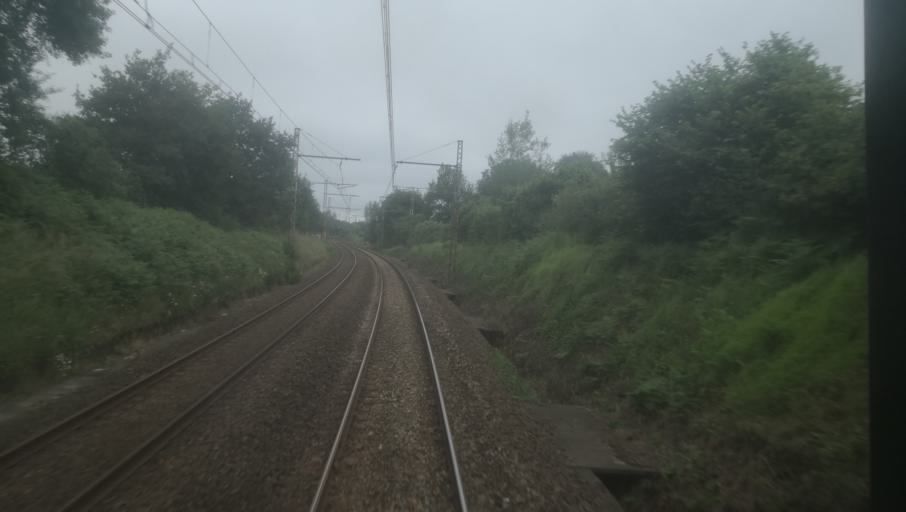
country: FR
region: Centre
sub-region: Departement de l'Indre
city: Chantome
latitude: 46.3629
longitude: 1.5403
